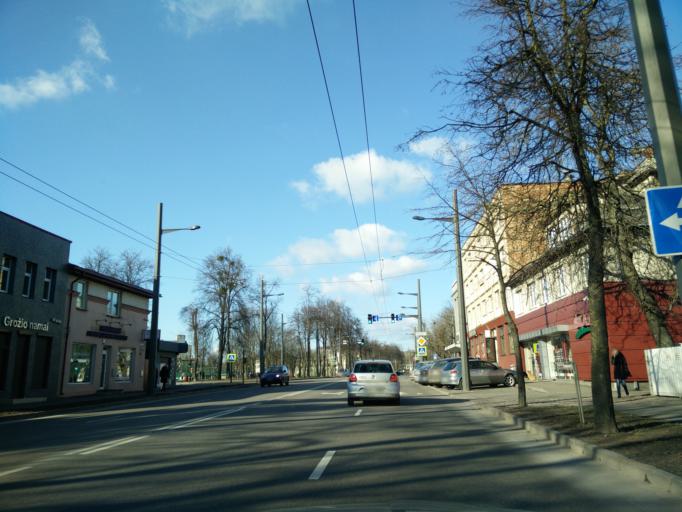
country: LT
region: Kauno apskritis
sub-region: Kaunas
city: Eiguliai
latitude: 54.9023
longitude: 23.9314
